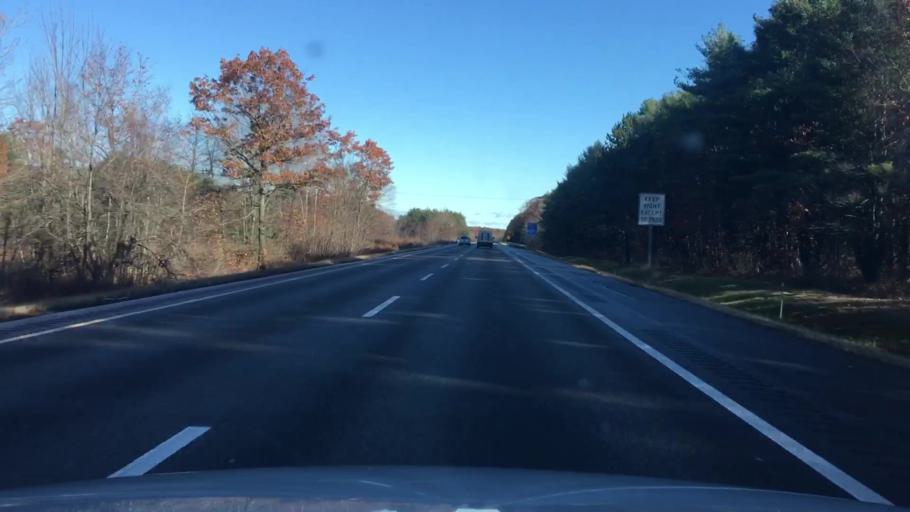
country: US
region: Maine
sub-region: Kennebec County
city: Augusta
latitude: 44.3660
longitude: -69.7760
